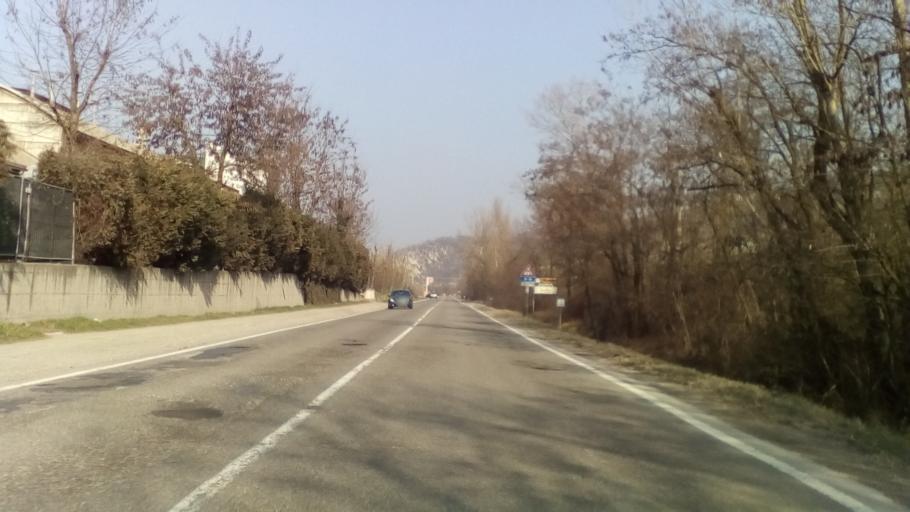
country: IT
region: Emilia-Romagna
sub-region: Provincia di Modena
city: Gorzano
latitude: 44.4694
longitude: 10.8424
